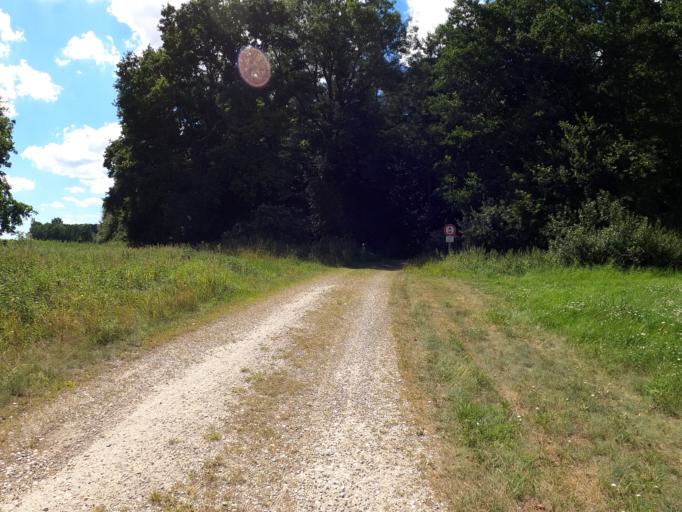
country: DE
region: Bavaria
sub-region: Swabia
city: Bubesheim
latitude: 48.4137
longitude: 10.2230
